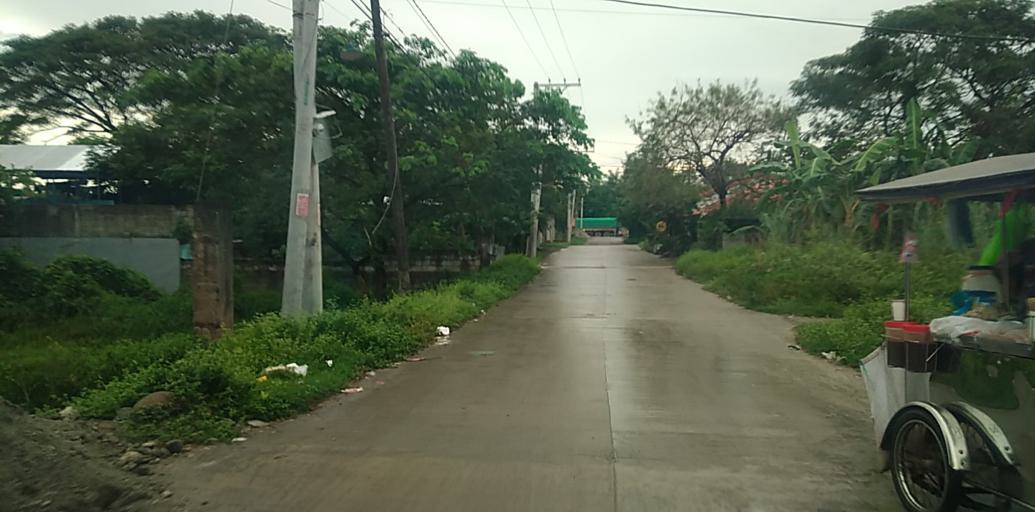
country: PH
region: Central Luzon
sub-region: Province of Pampanga
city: Arayat
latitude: 15.1514
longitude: 120.7480
